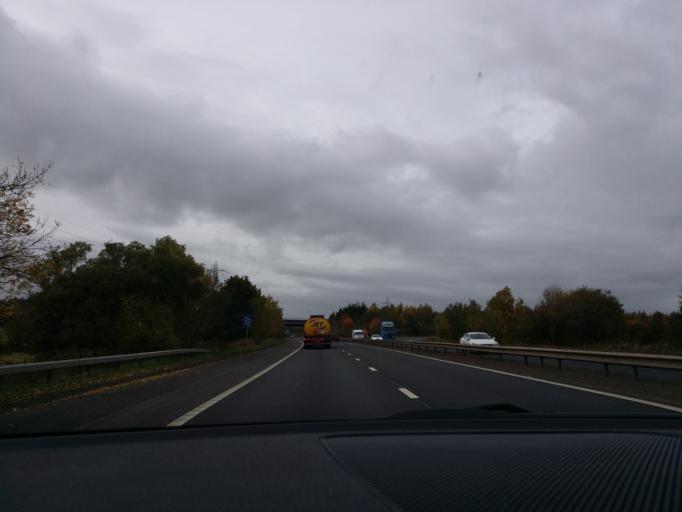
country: GB
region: Scotland
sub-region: Falkirk
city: Airth
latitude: 56.0418
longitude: -3.7789
